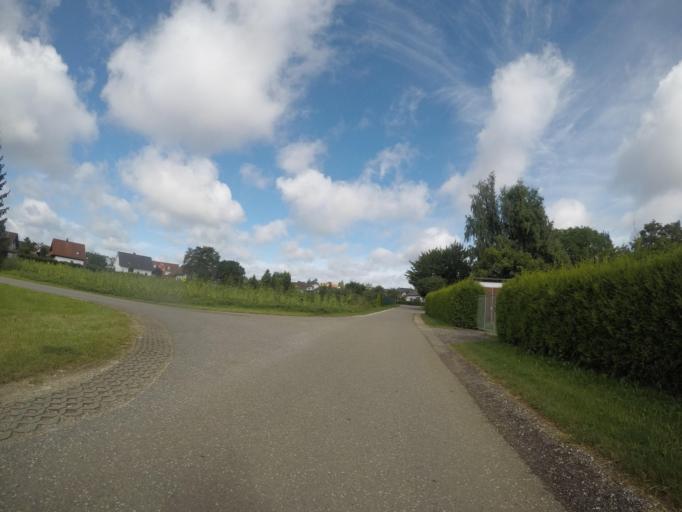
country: DE
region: Baden-Wuerttemberg
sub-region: Tuebingen Region
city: Laichingen
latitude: 48.4393
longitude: 9.6565
